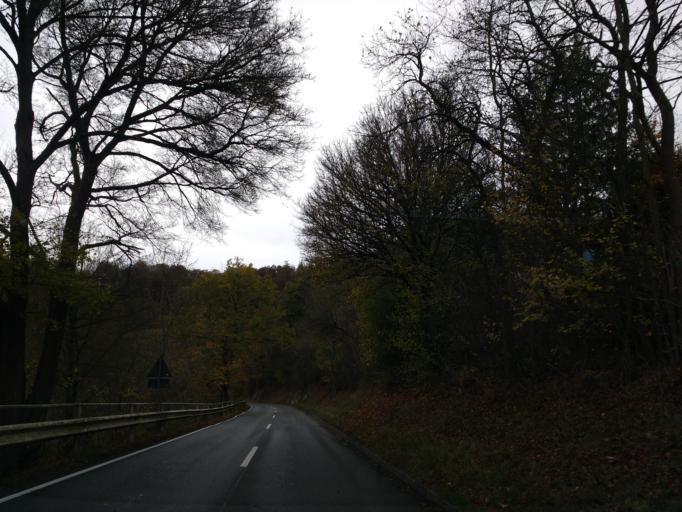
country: DE
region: Hesse
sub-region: Regierungsbezirk Kassel
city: Sachsenhausen
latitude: 51.2068
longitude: 9.0038
